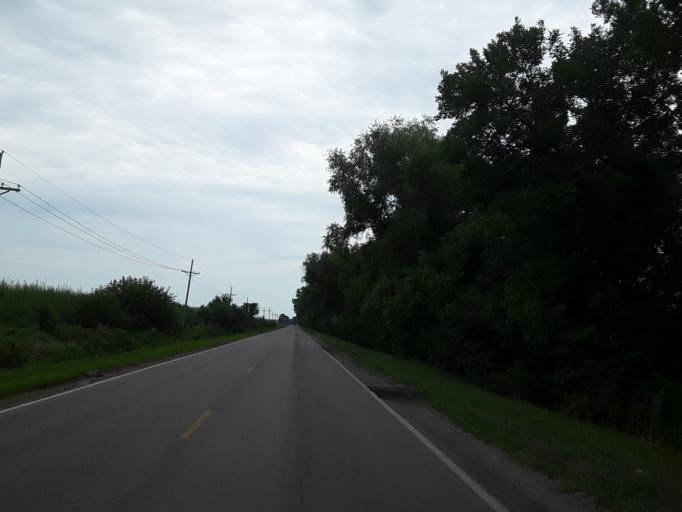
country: US
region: Nebraska
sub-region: Saunders County
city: Yutan
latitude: 41.2304
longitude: -96.3304
